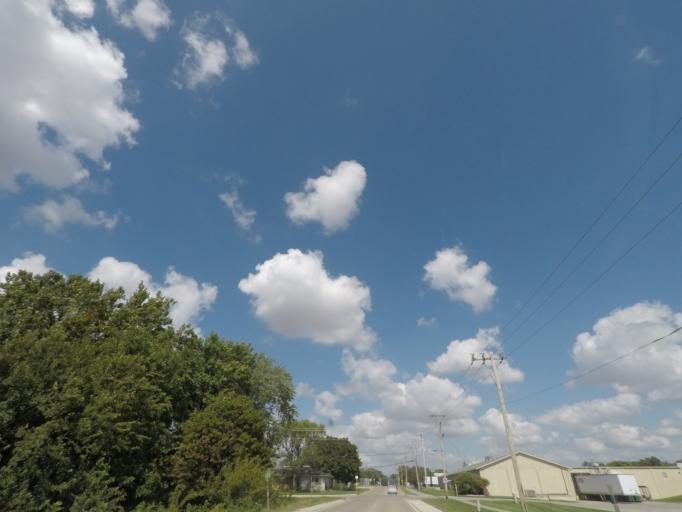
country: US
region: Iowa
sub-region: Story County
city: Nevada
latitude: 42.0126
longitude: -93.4445
